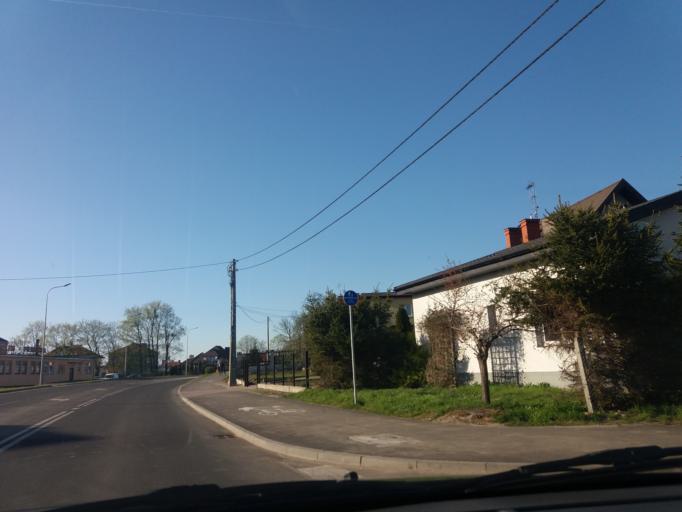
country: PL
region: Warmian-Masurian Voivodeship
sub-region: Powiat nidzicki
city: Nidzica
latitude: 53.3700
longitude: 20.4289
